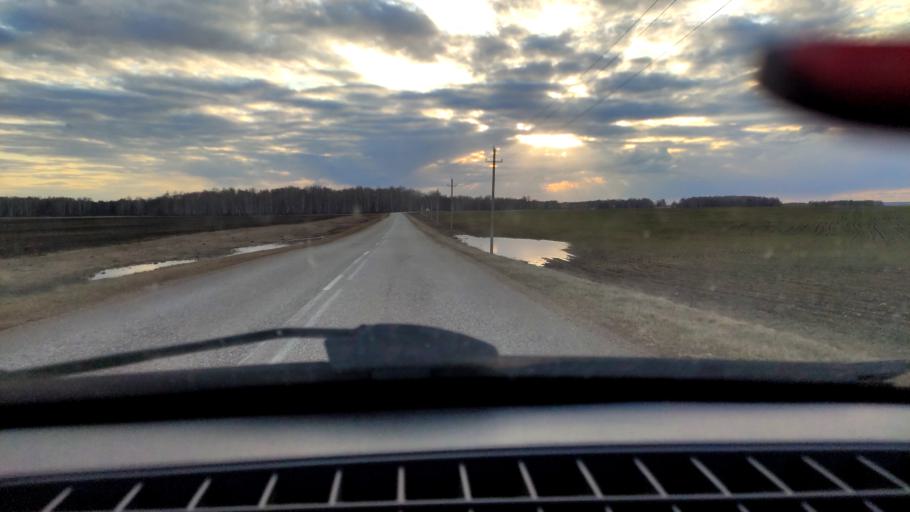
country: RU
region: Bashkortostan
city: Tolbazy
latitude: 54.0039
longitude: 55.6227
